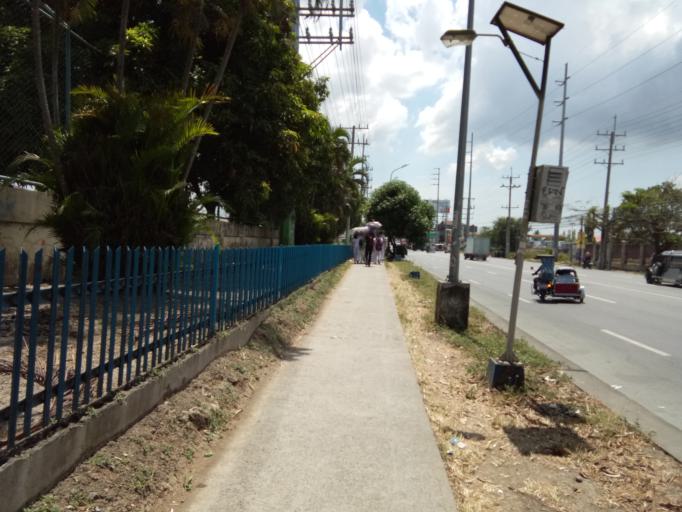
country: PH
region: Calabarzon
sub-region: Province of Cavite
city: Manggahan
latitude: 14.2919
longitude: 120.9143
